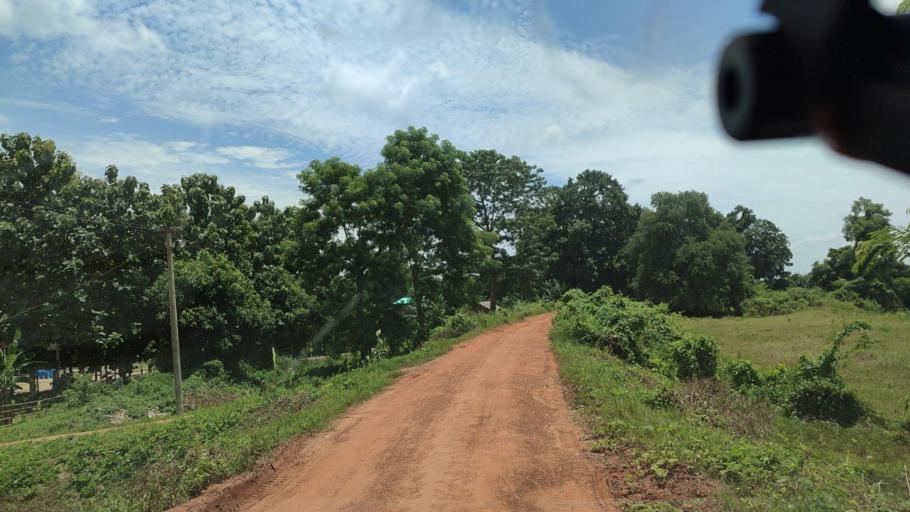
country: MM
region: Bago
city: Letpandan
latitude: 17.7815
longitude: 95.6044
